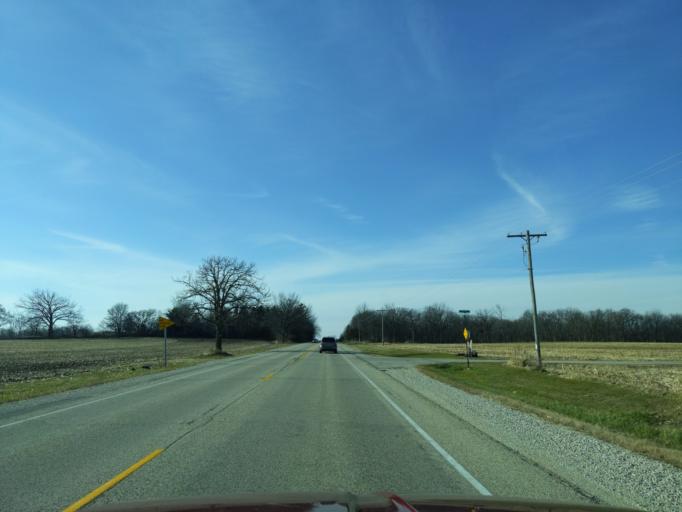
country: US
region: Wisconsin
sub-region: Walworth County
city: Whitewater
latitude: 42.8279
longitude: -88.8087
